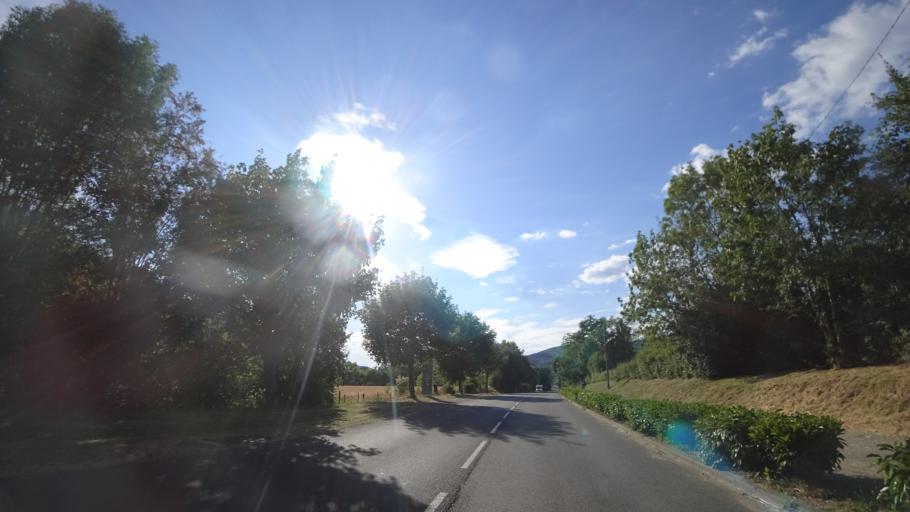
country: FR
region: Languedoc-Roussillon
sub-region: Departement de la Lozere
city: La Canourgue
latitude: 44.4344
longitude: 3.2052
